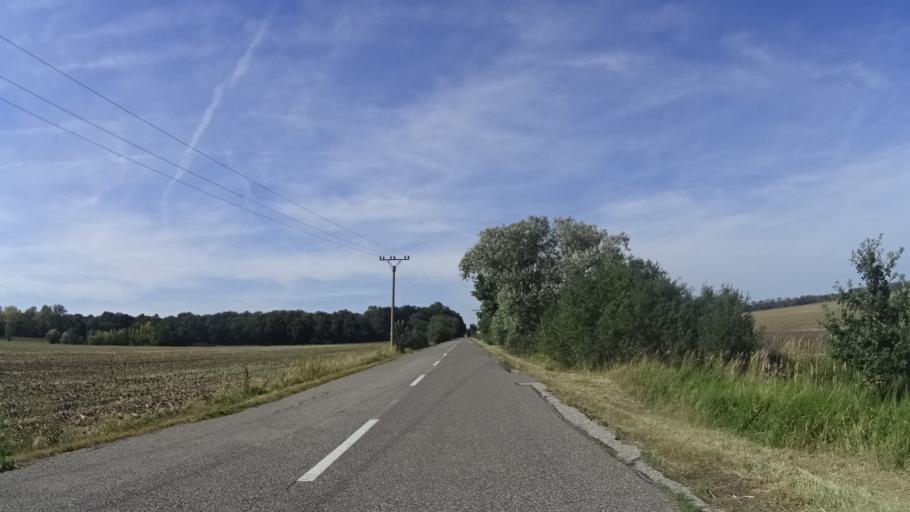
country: AT
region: Lower Austria
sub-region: Politischer Bezirk Ganserndorf
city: Angern an der March
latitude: 48.3919
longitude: 16.8642
